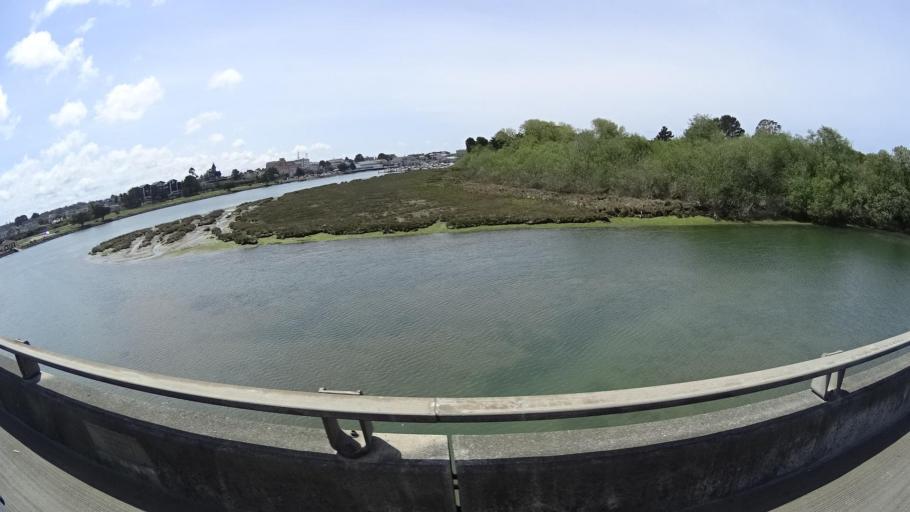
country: US
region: California
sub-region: Humboldt County
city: Eureka
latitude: 40.8105
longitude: -124.1560
